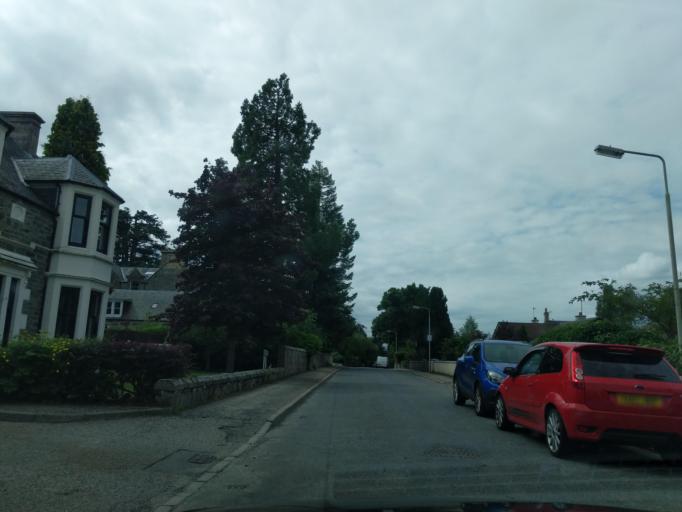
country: GB
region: Scotland
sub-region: Highland
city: Grantown on Spey
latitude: 57.3268
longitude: -3.6099
